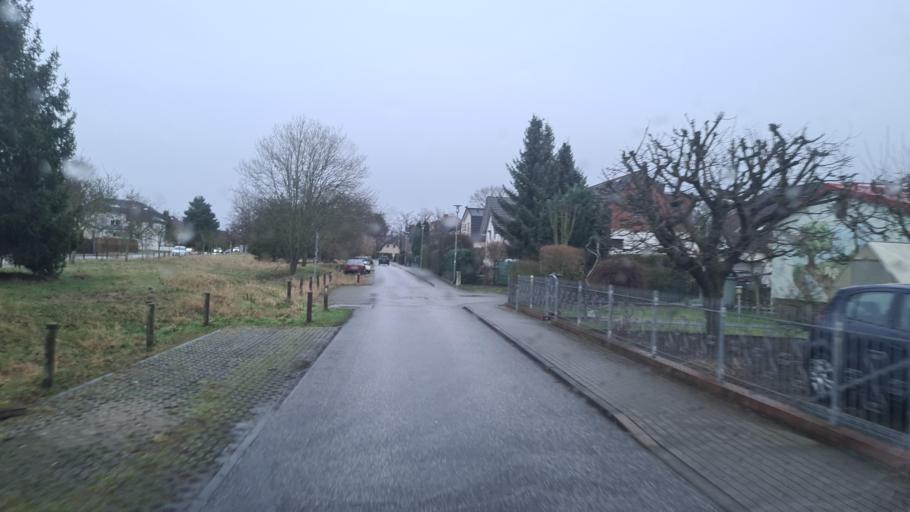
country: DE
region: Brandenburg
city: Teltow
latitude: 52.3891
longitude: 13.2849
